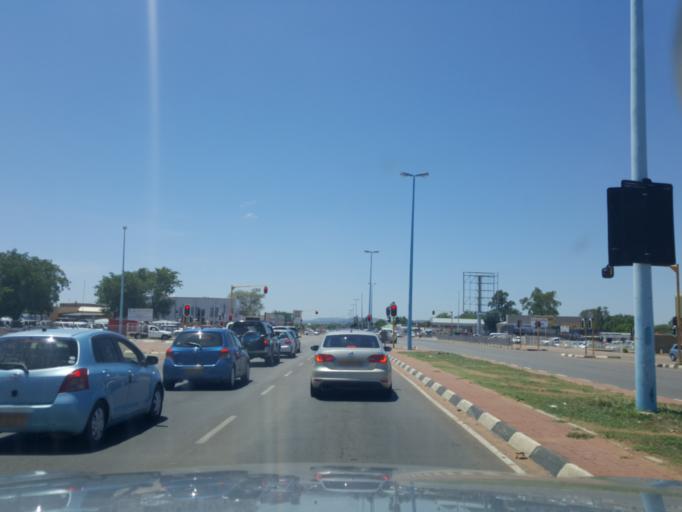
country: BW
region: Kweneng
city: Mogoditshane
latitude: -24.6281
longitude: 25.8713
